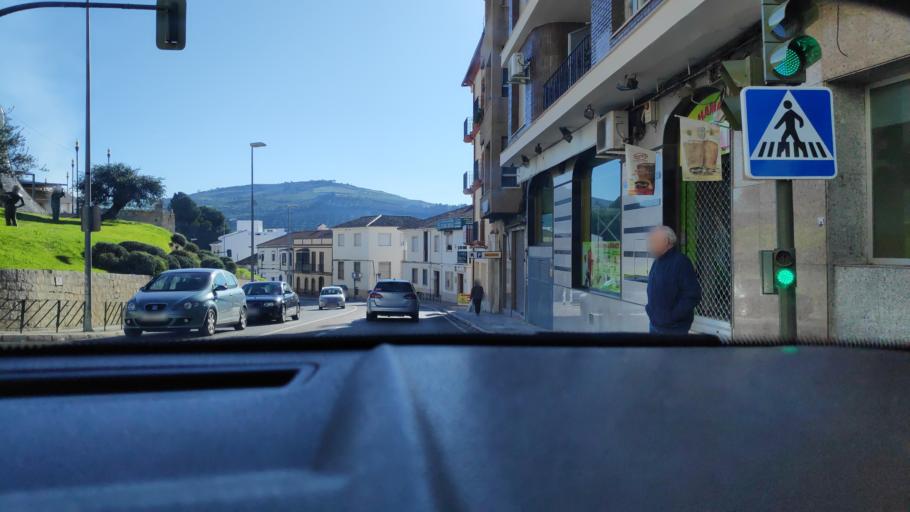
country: ES
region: Andalusia
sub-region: Province of Cordoba
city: Baena
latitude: 37.6157
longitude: -4.3228
